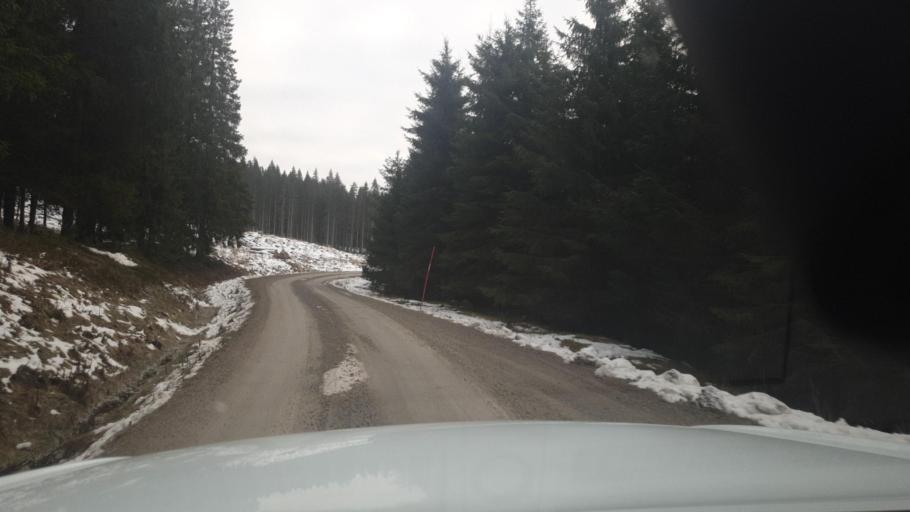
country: SE
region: Vaermland
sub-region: Sunne Kommun
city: Sunne
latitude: 59.8596
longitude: 12.8820
